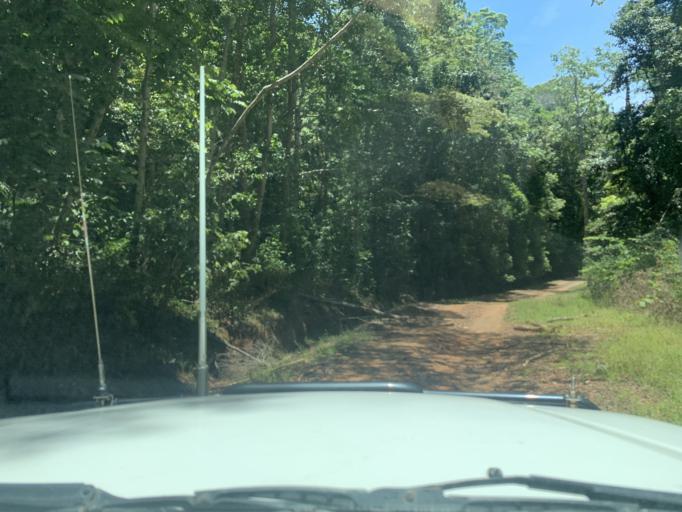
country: AU
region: Queensland
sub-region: Cairns
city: Redlynch
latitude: -16.9592
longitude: 145.6442
